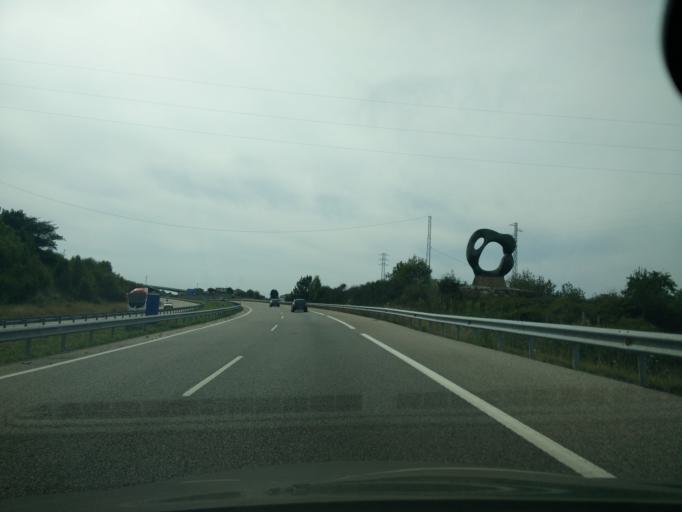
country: ES
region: Asturias
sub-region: Province of Asturias
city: Arriba
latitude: 43.5080
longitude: -5.5486
